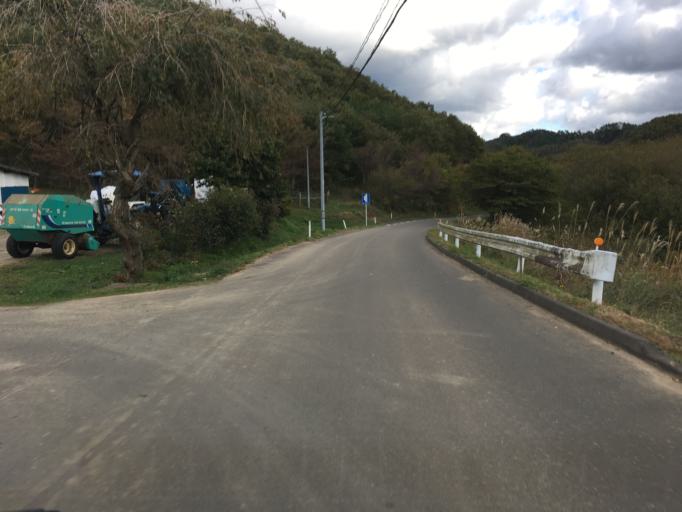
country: JP
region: Miyagi
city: Marumori
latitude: 37.8201
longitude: 140.7559
